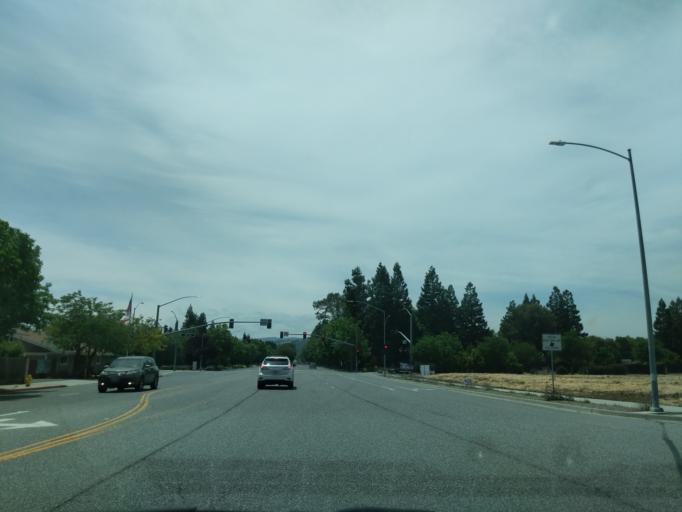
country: US
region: California
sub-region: Santa Clara County
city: Morgan Hill
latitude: 37.1389
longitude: -121.6144
